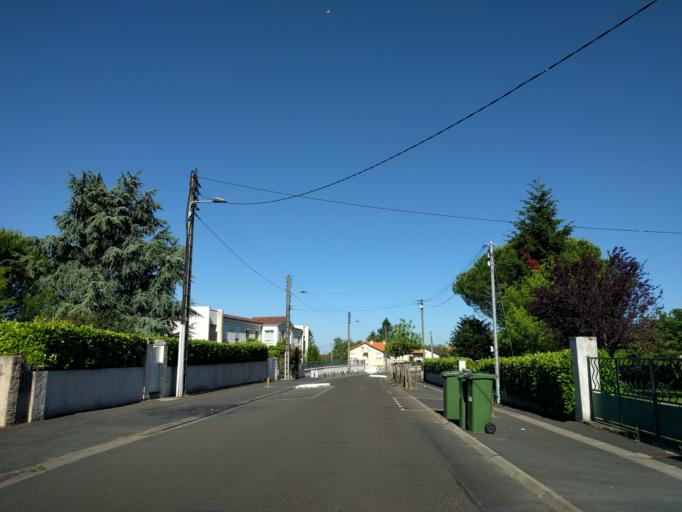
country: FR
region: Poitou-Charentes
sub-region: Departement des Deux-Sevres
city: Niort
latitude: 46.3377
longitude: -0.4319
